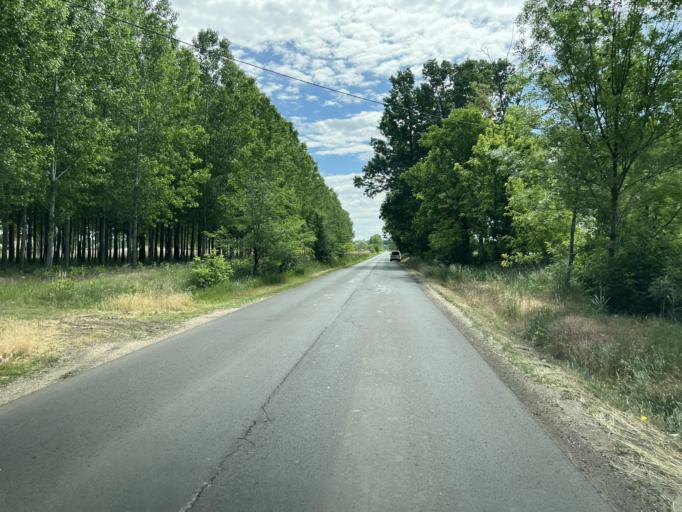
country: HU
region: Pest
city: Szentlorinckata
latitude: 47.5110
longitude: 19.7504
